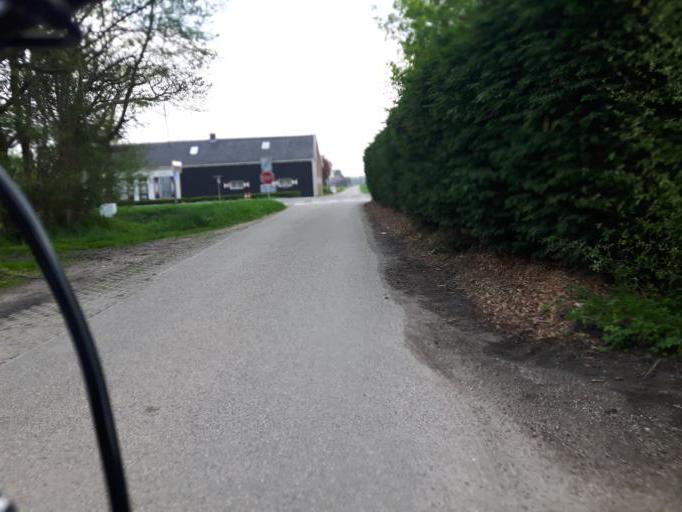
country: NL
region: Zeeland
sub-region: Gemeente Borsele
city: Borssele
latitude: 51.4638
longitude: 3.7990
